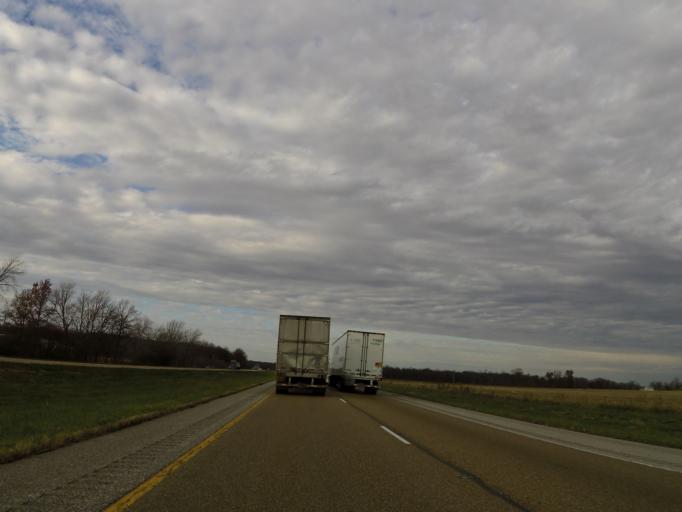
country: US
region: Illinois
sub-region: Washington County
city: Nashville
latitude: 38.3912
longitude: -89.2886
